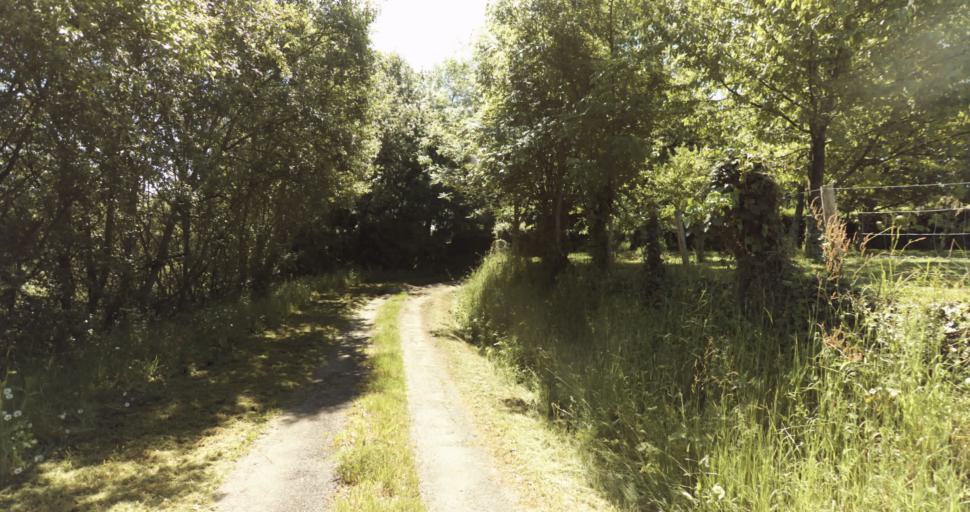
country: FR
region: Limousin
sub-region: Departement de la Haute-Vienne
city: Le Vigen
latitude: 45.7429
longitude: 1.2937
